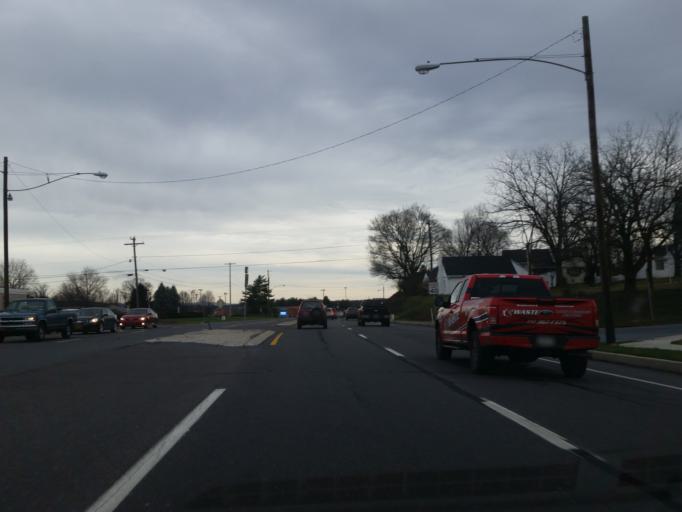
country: US
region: Pennsylvania
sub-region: Dauphin County
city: Paxtonia
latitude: 40.3230
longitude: -76.7872
